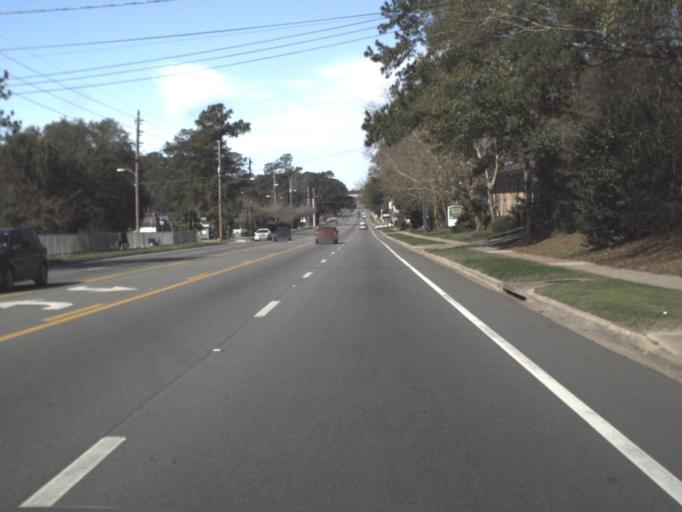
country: US
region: Florida
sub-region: Leon County
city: Tallahassee
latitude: 30.4409
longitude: -84.3226
